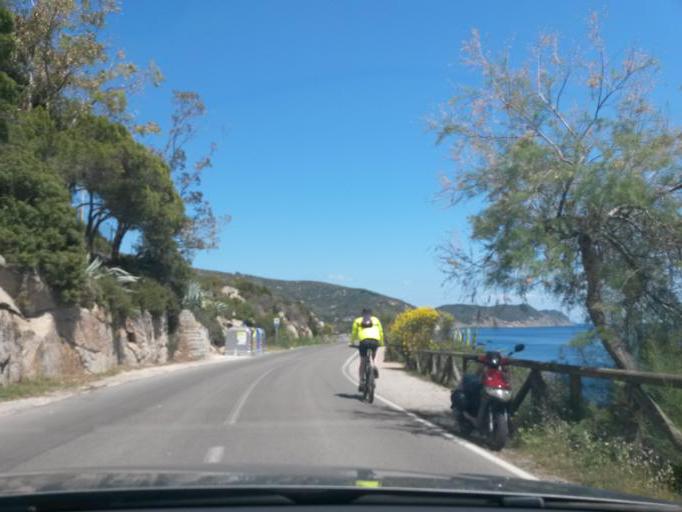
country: IT
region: Tuscany
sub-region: Provincia di Livorno
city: Marciana
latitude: 42.7329
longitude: 10.1654
